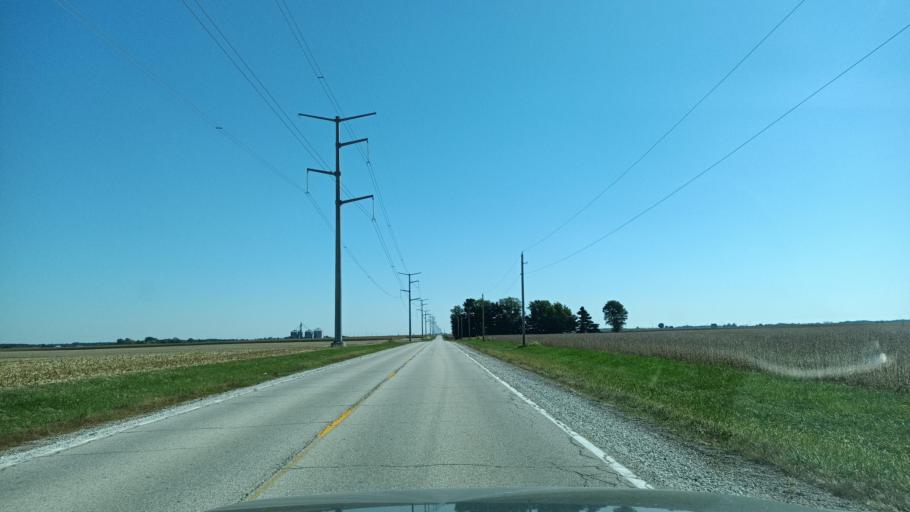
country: US
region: Illinois
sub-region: Peoria County
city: Elmwood
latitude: 40.9024
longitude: -90.0357
